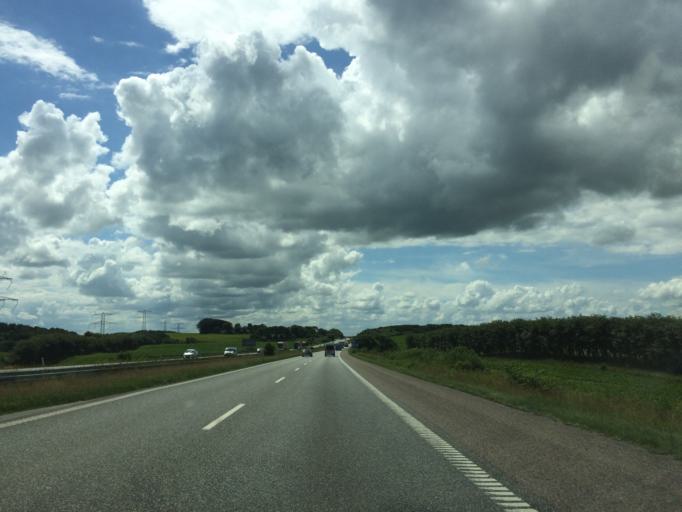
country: DK
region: North Denmark
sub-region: Rebild Kommune
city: Stovring
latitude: 56.8494
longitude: 9.7555
